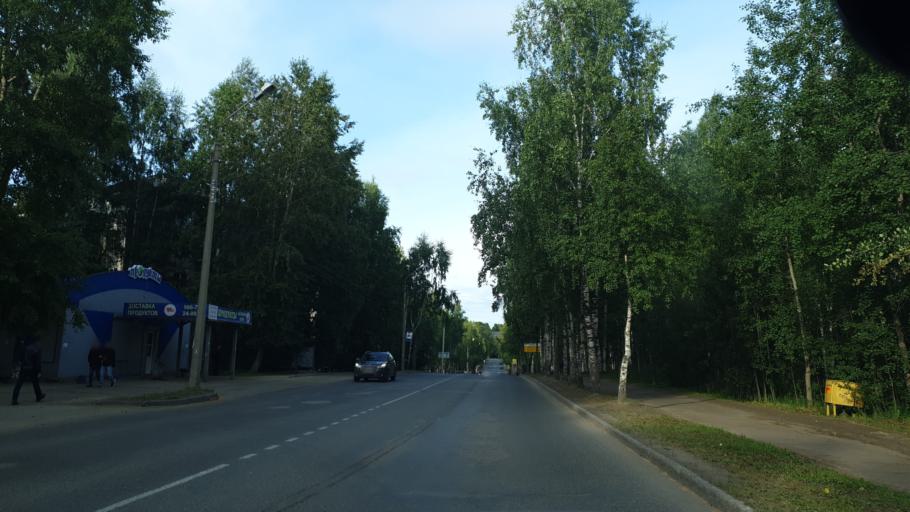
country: RU
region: Komi Republic
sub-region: Syktyvdinskiy Rayon
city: Syktyvkar
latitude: 61.6581
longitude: 50.8107
